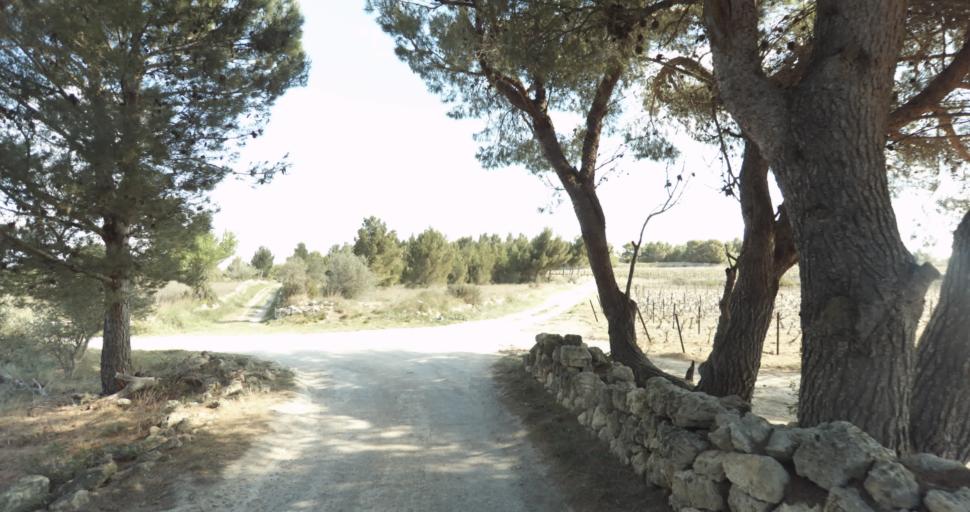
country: FR
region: Languedoc-Roussillon
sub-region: Departement de l'Aude
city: Leucate
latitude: 42.9291
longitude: 3.0309
